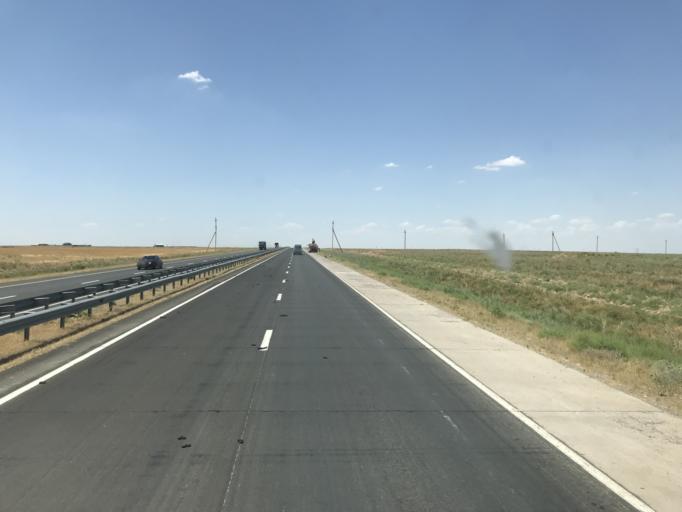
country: KZ
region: Ongtustik Qazaqstan
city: Temirlanovka
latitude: 42.5247
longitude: 69.3737
